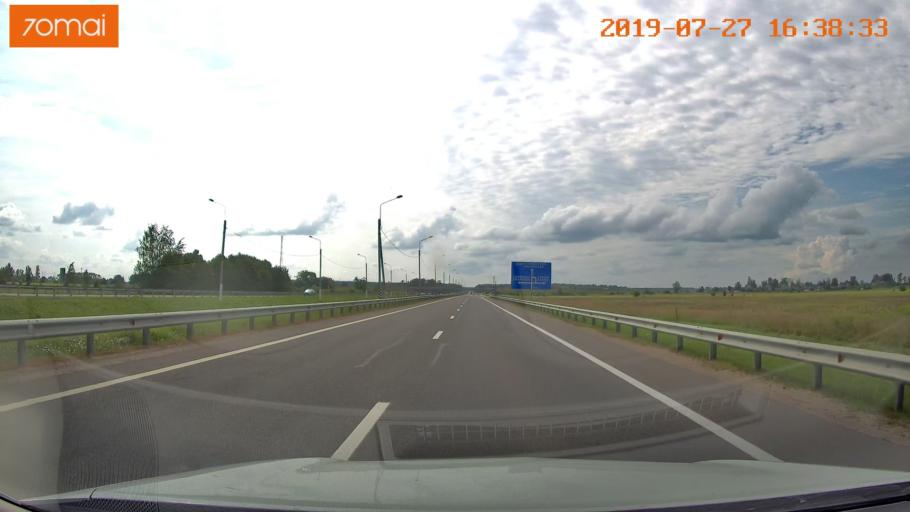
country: RU
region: Kaliningrad
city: Gvardeysk
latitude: 54.6489
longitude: 21.2253
